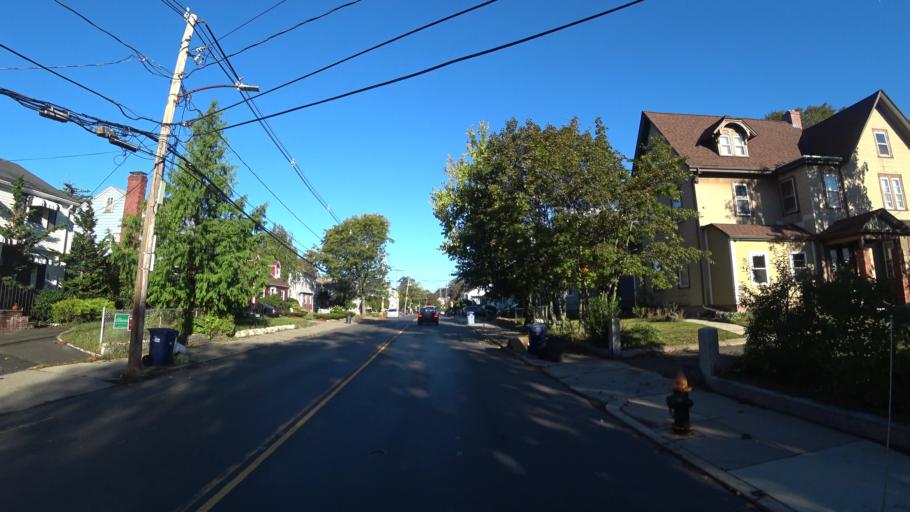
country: US
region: Massachusetts
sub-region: Middlesex County
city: Watertown
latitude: 42.3542
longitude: -71.1548
